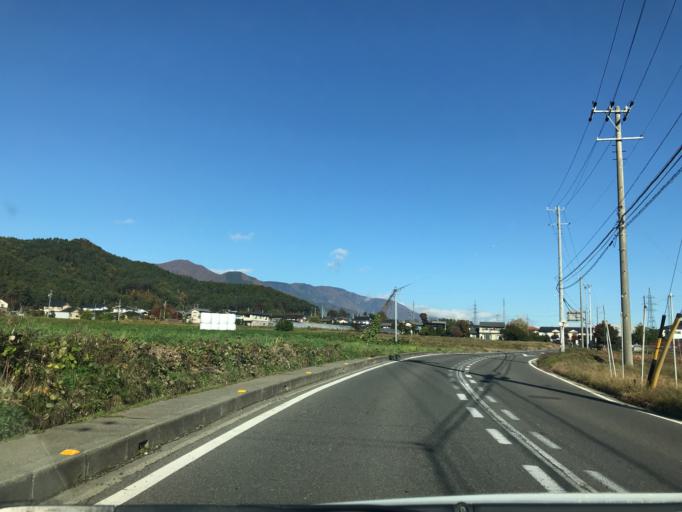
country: JP
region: Nagano
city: Matsumoto
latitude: 36.1702
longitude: 137.8719
